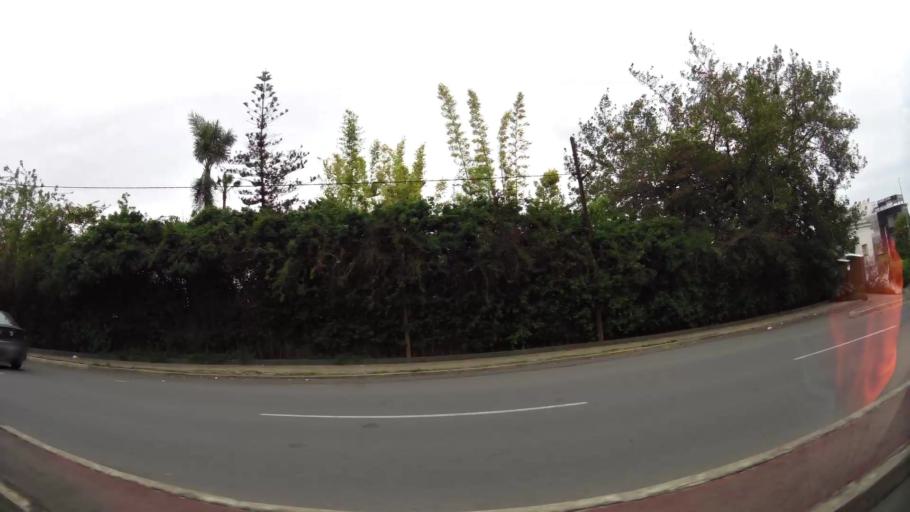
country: MA
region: Grand Casablanca
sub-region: Casablanca
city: Casablanca
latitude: 33.5630
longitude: -7.6145
